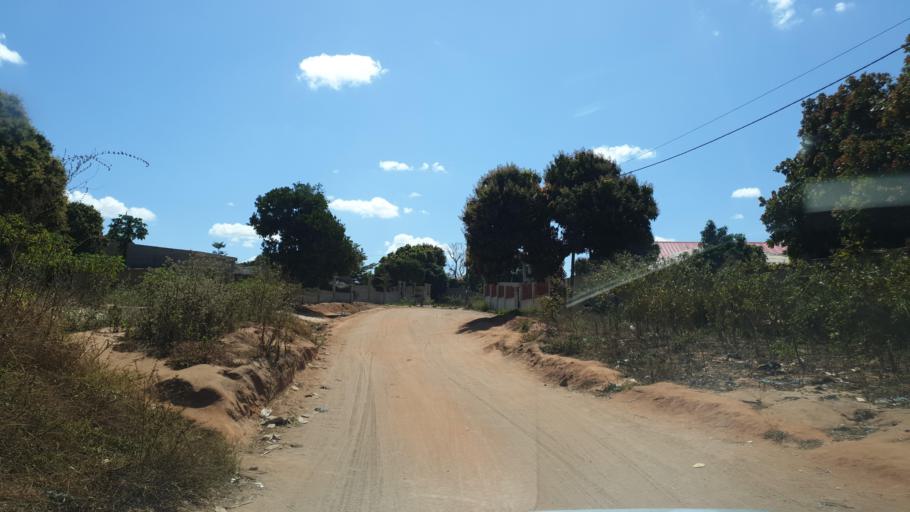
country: MZ
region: Nampula
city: Nampula
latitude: -15.1001
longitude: 39.2078
